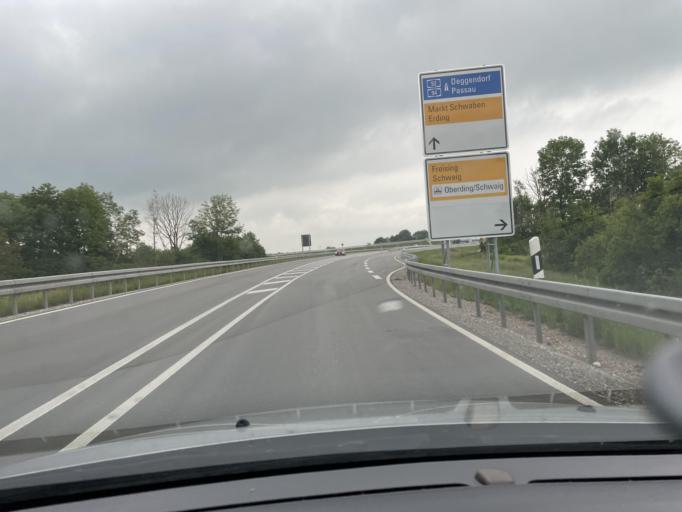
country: DE
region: Bavaria
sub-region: Upper Bavaria
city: Oberding
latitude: 48.3623
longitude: 11.8301
